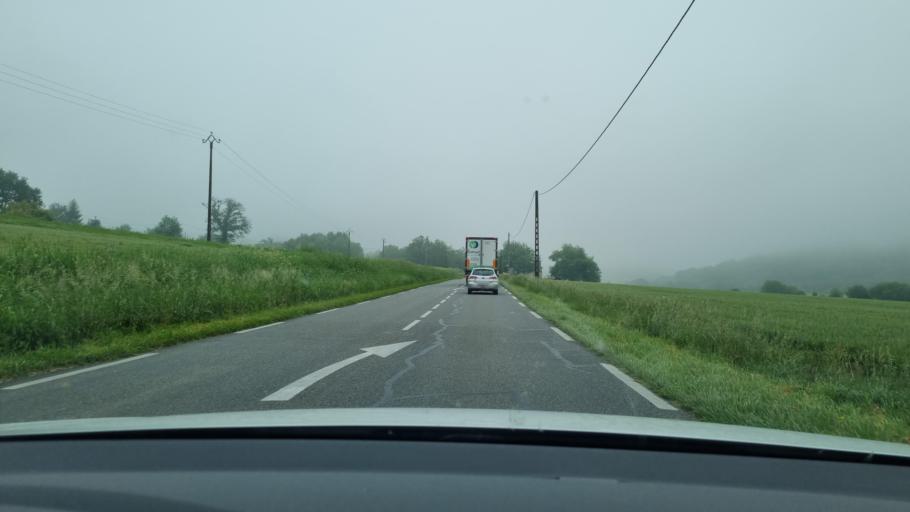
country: FR
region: Aquitaine
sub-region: Departement des Pyrenees-Atlantiques
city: Orthez
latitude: 43.5068
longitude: -0.7367
